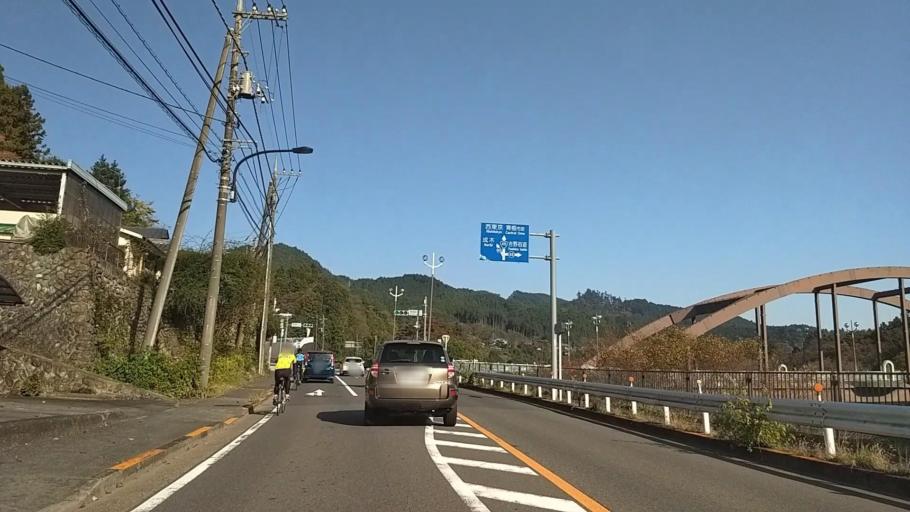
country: JP
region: Tokyo
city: Ome
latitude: 35.8056
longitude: 139.2068
